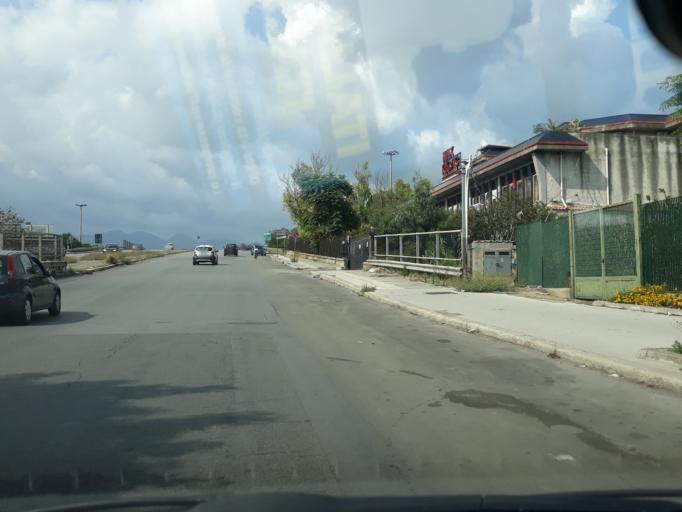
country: IT
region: Sicily
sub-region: Palermo
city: Palermo
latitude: 38.0952
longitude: 13.3413
